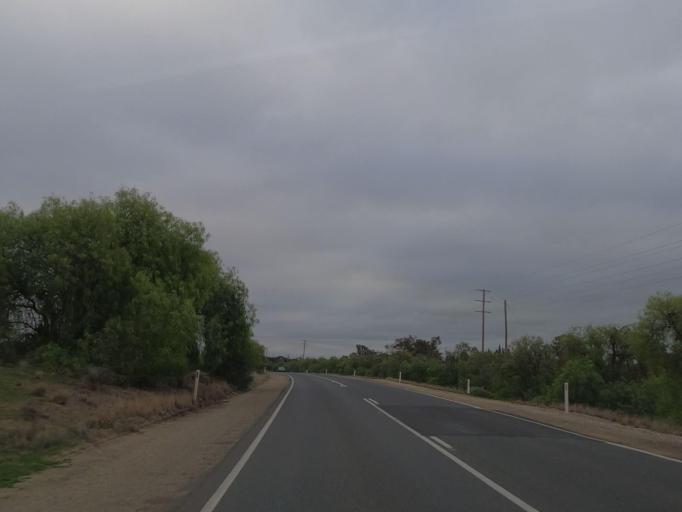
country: AU
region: Victoria
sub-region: Swan Hill
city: Swan Hill
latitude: -35.4461
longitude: 143.6203
